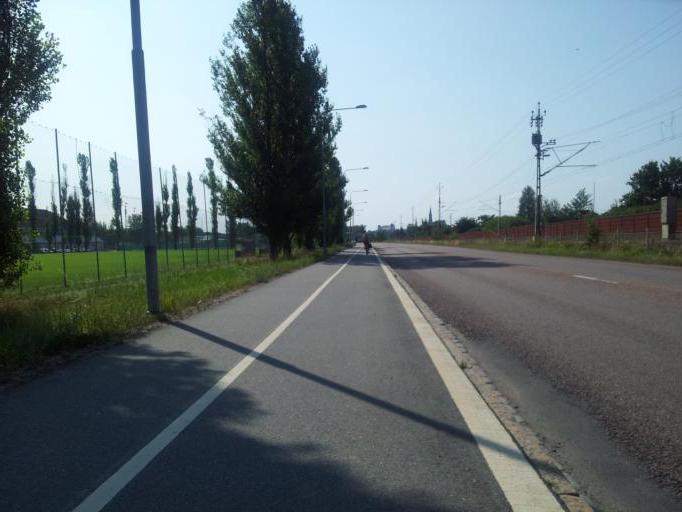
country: SE
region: Uppsala
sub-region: Uppsala Kommun
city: Uppsala
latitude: 59.8780
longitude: 17.6357
